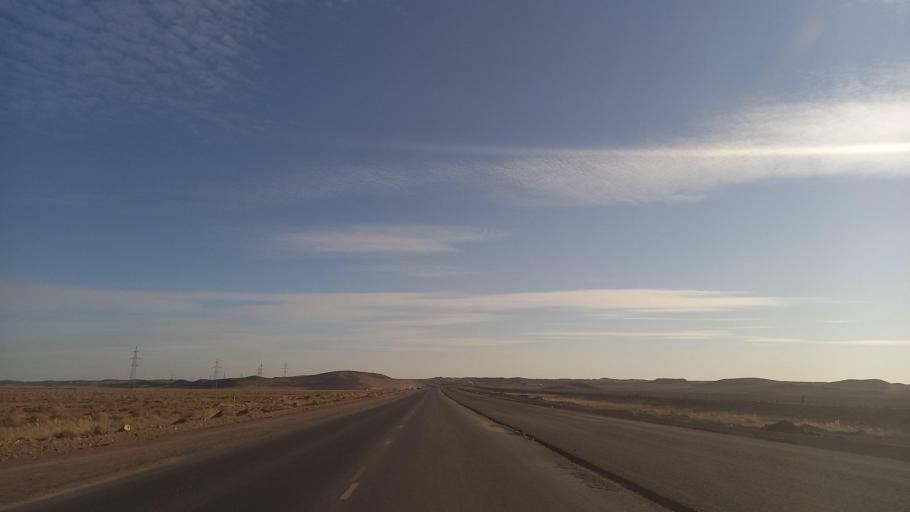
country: KZ
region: Zhambyl
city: Mynaral
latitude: 45.3803
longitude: 73.6530
